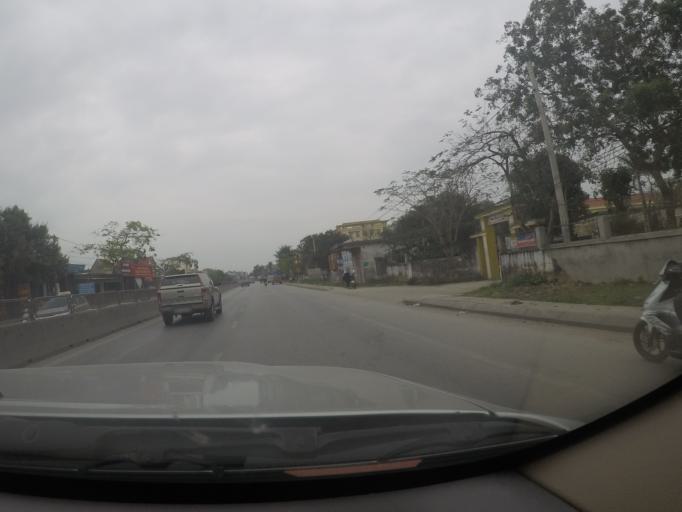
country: VN
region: Nghe An
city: Dien Chau
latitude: 19.0157
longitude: 105.5858
